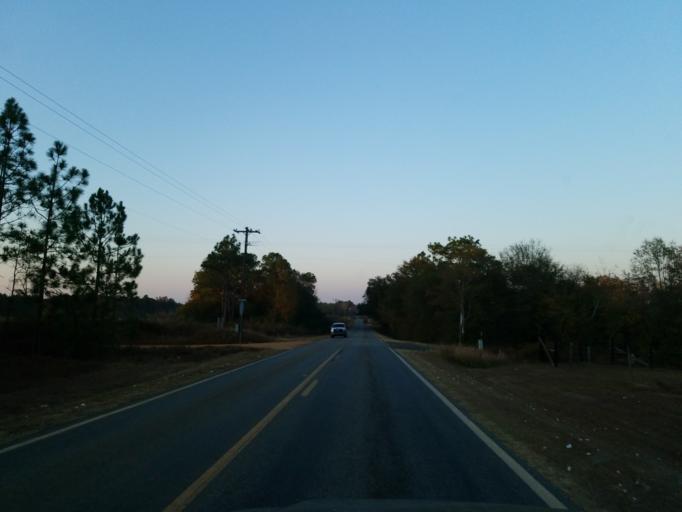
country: US
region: Georgia
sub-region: Ben Hill County
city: Fitzgerald
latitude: 31.6857
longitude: -83.3853
